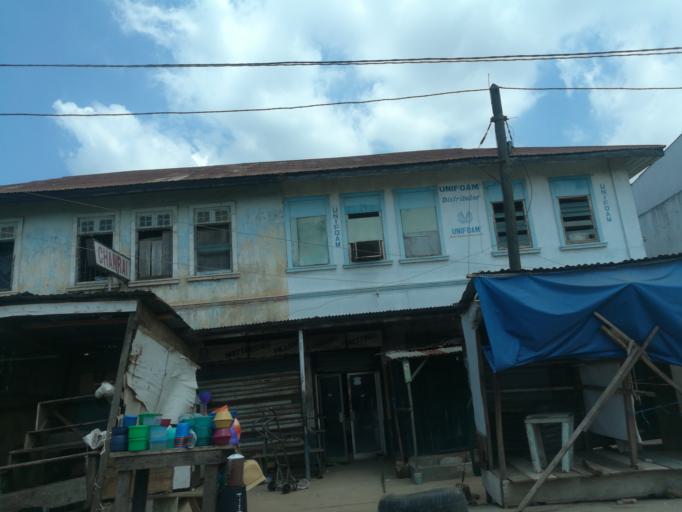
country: NG
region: Oyo
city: Ibadan
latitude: 7.3875
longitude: 3.8835
